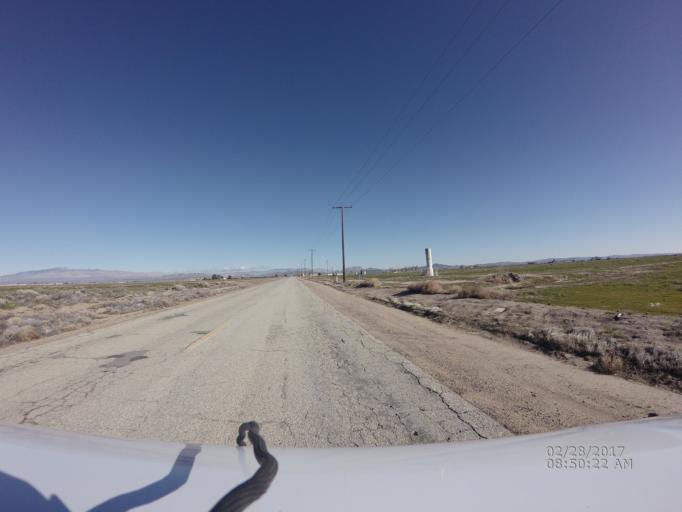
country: US
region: California
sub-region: Kern County
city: Rosamond
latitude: 34.7942
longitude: -118.2376
